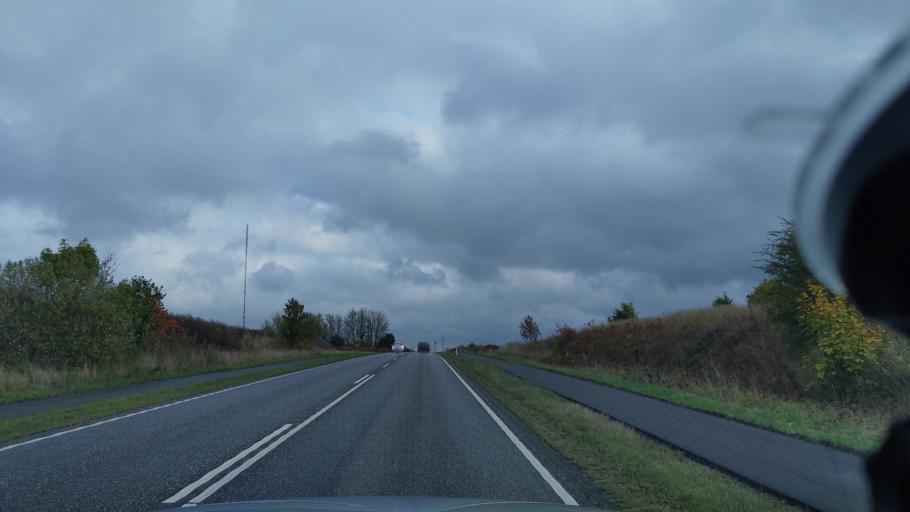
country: DK
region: Zealand
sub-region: Naestved Kommune
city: Fensmark
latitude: 55.2538
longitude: 11.7956
